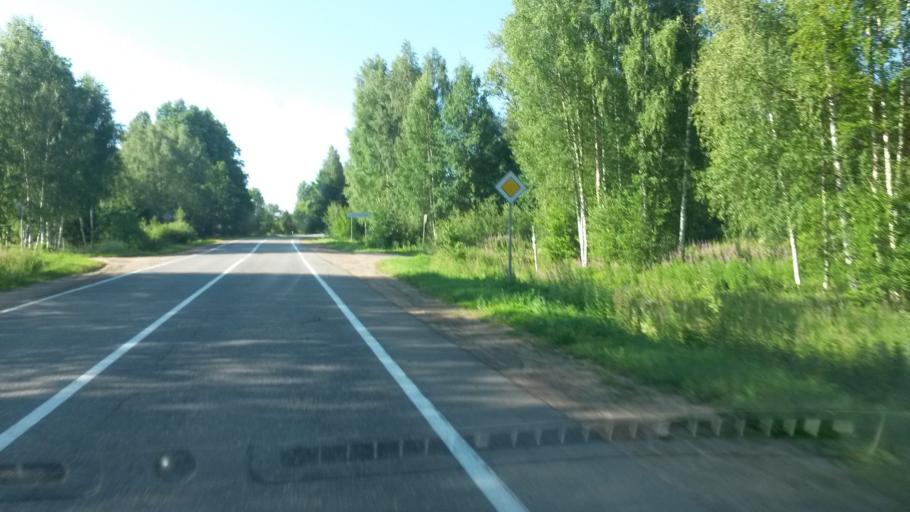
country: RU
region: Jaroslavl
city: Gavrilov-Yam
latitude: 57.2840
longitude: 39.9535
